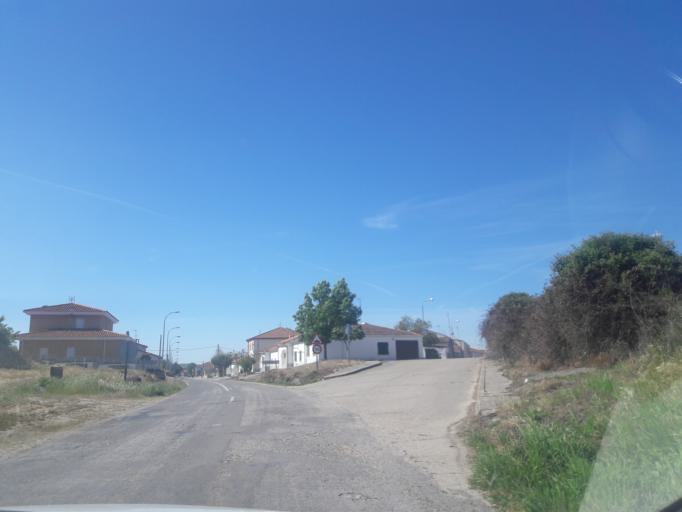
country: ES
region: Castille and Leon
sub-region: Provincia de Salamanca
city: Lumbrales
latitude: 40.9418
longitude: -6.7168
